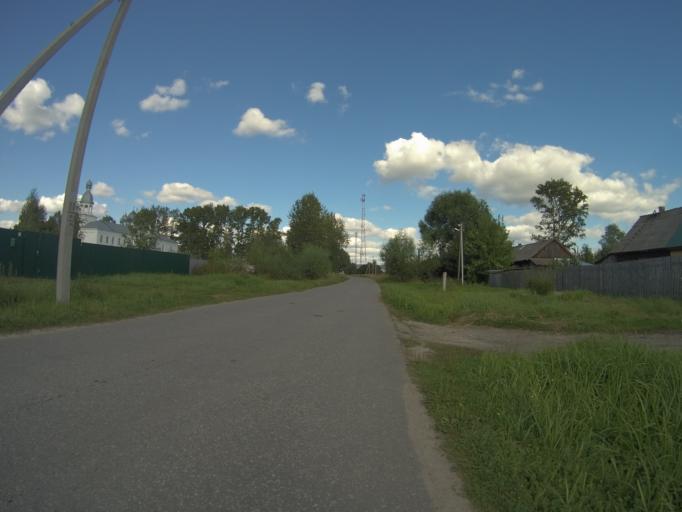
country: RU
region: Vladimir
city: Urshel'skiy
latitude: 55.6767
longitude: 40.2098
